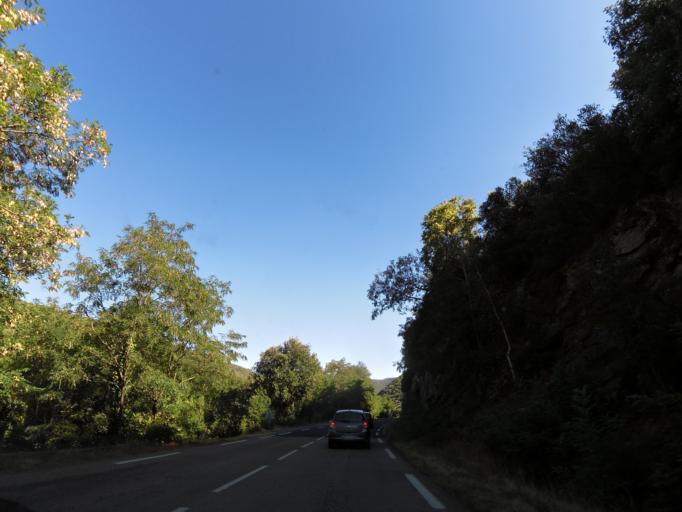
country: FR
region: Languedoc-Roussillon
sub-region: Departement du Gard
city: Valleraugue
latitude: 44.0363
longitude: 3.6759
